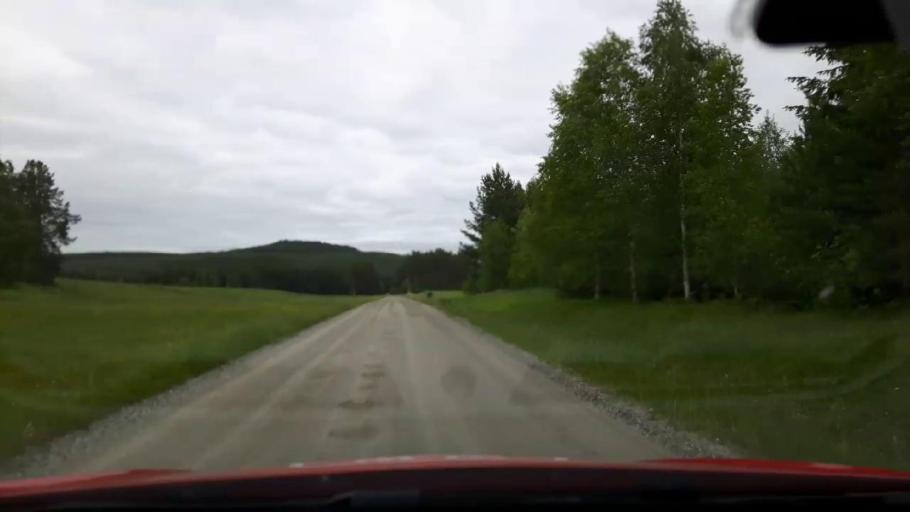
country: SE
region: Jaemtland
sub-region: Ragunda Kommun
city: Hammarstrand
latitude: 63.2115
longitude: 16.0922
